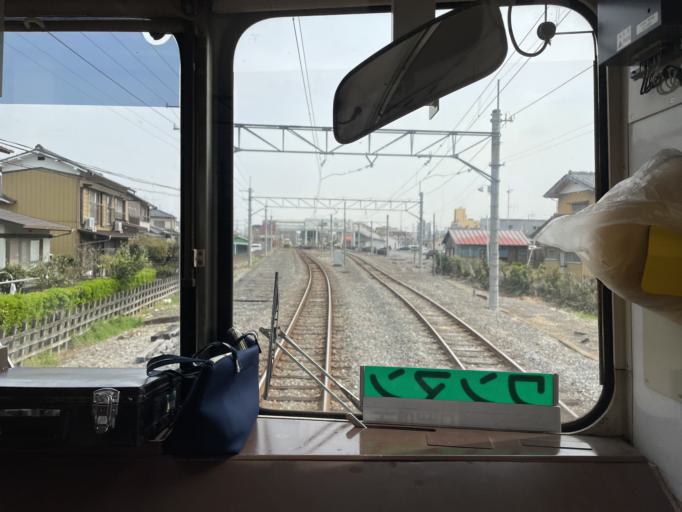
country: JP
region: Saitama
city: Gyoda
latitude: 36.1438
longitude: 139.4568
